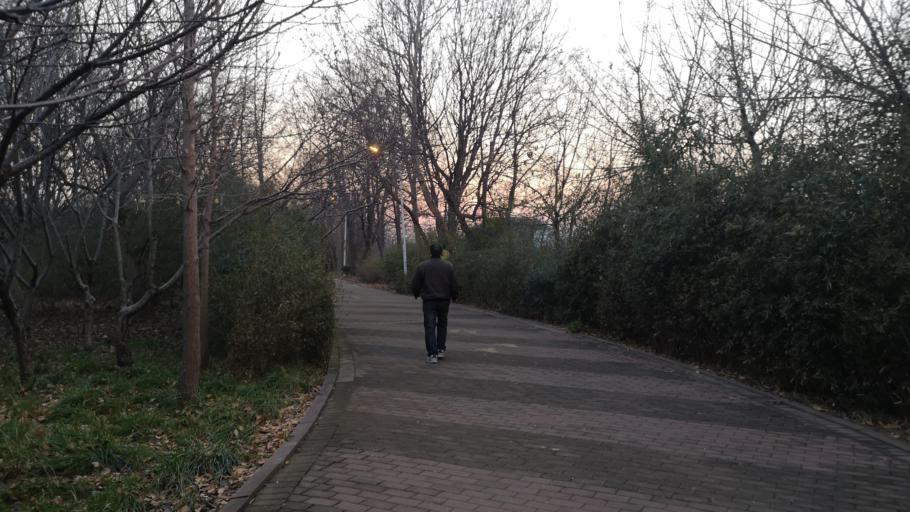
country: CN
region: Henan Sheng
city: Zhongyuanlu
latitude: 35.7433
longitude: 115.0615
